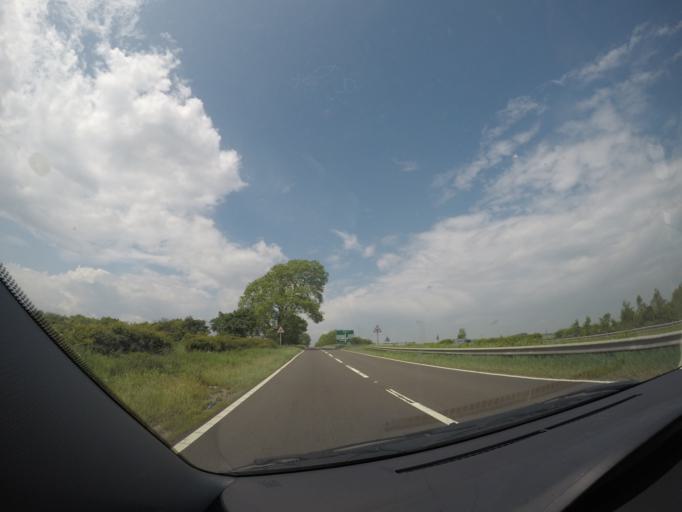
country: GB
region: England
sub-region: North Yorkshire
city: Catterick Garrison
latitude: 54.4582
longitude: -1.7185
